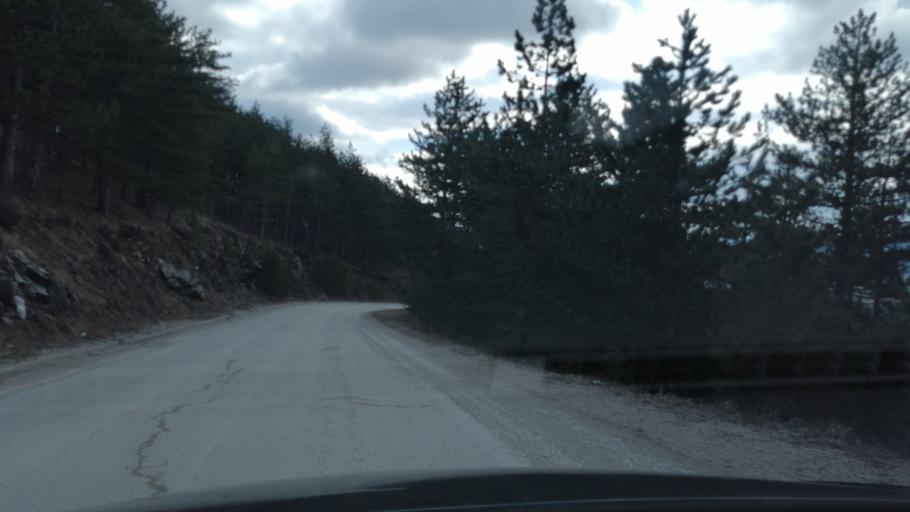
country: RS
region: Central Serbia
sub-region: Zlatiborski Okrug
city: Bajina Basta
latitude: 43.8738
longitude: 19.5667
